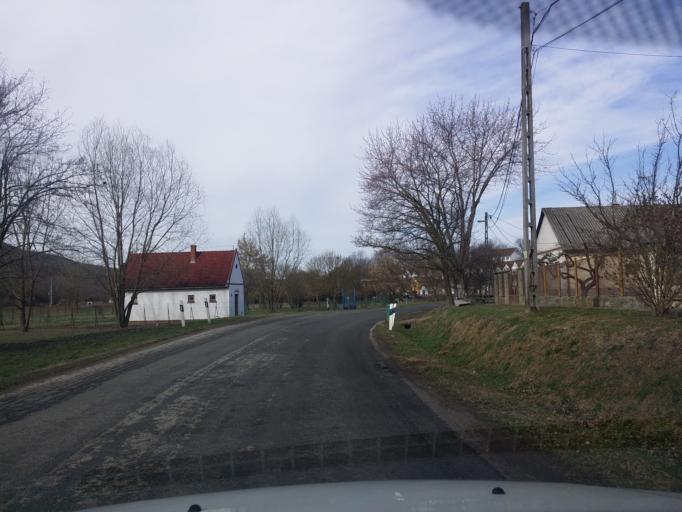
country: HU
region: Baranya
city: Villany
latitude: 45.8804
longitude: 18.4318
